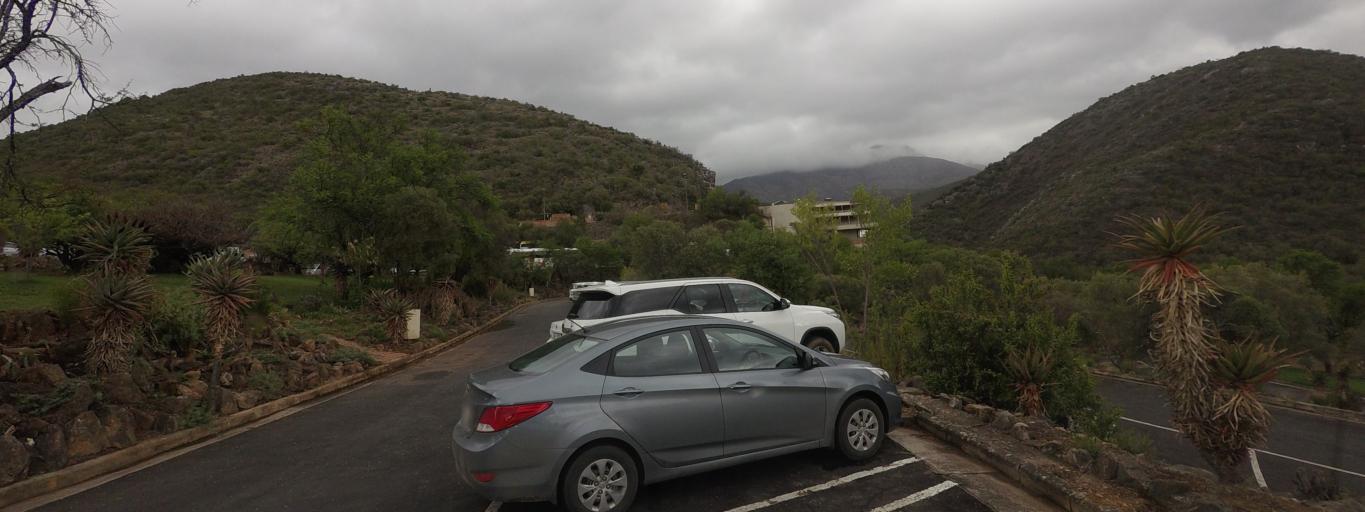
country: ZA
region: Western Cape
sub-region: Eden District Municipality
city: Oudtshoorn
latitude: -33.3940
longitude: 22.2148
